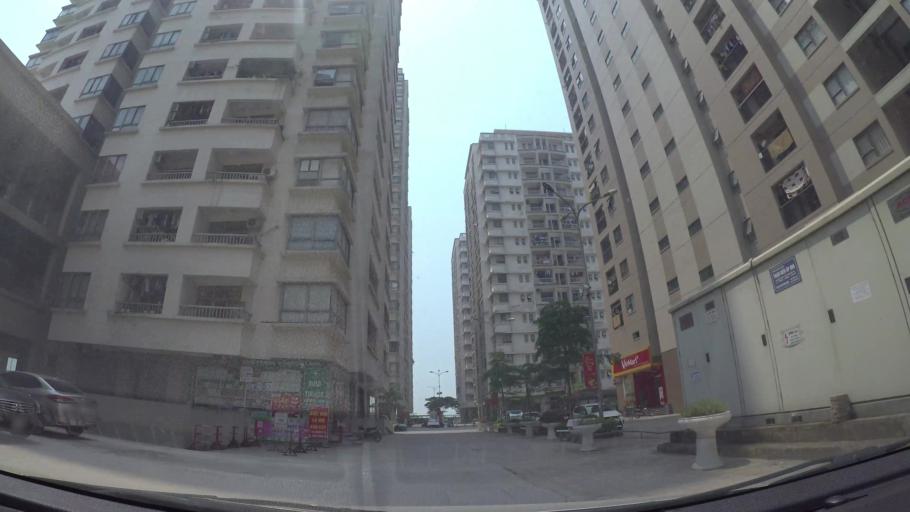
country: VN
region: Ha Noi
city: Thanh Xuan
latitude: 20.9952
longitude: 105.7848
